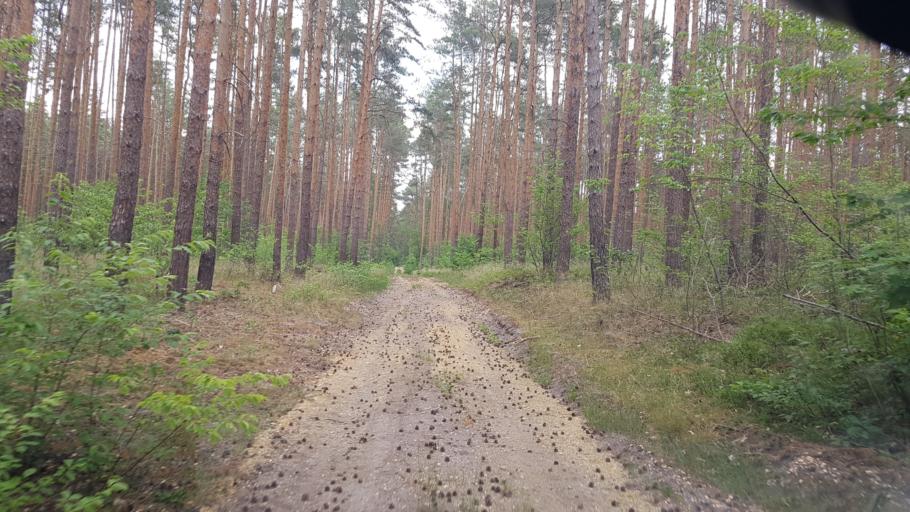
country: DE
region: Brandenburg
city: Hohenleipisch
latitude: 51.5114
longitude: 13.5702
